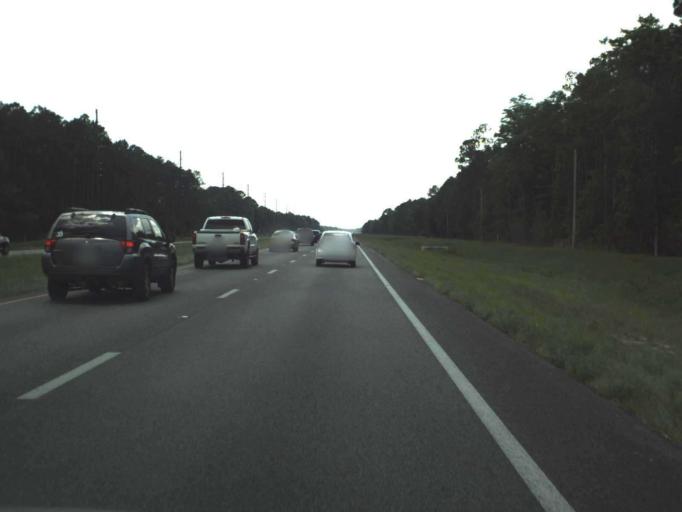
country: US
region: Florida
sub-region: Volusia County
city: Samsula-Spruce Creek
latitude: 29.0121
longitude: -81.0262
